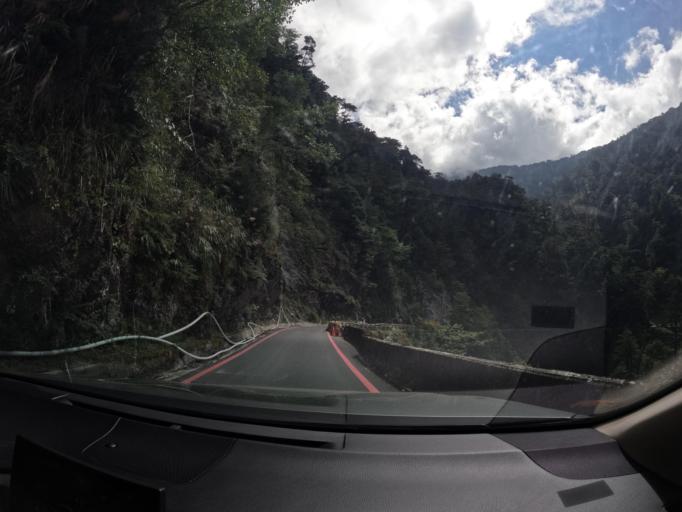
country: TW
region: Taiwan
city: Yujing
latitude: 23.2593
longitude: 120.9215
